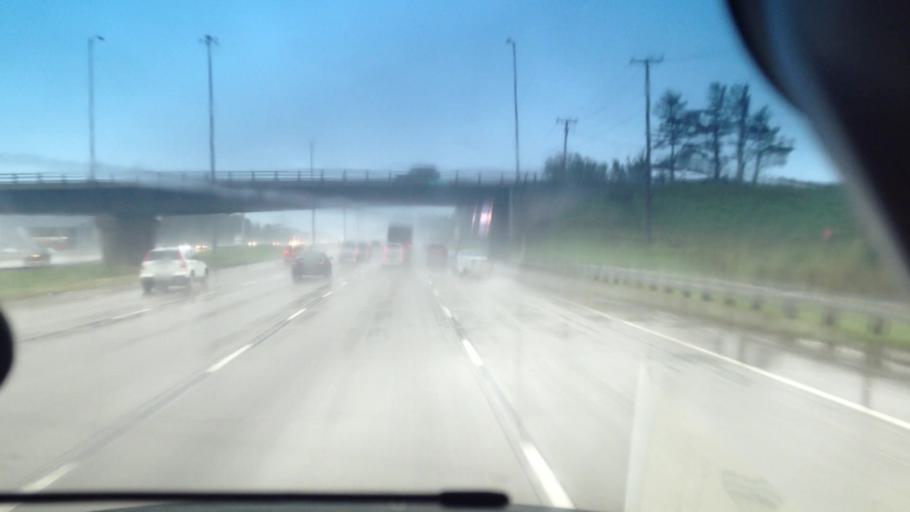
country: CA
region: Quebec
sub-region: Laurentides
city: Blainville
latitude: 45.6767
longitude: -73.9140
